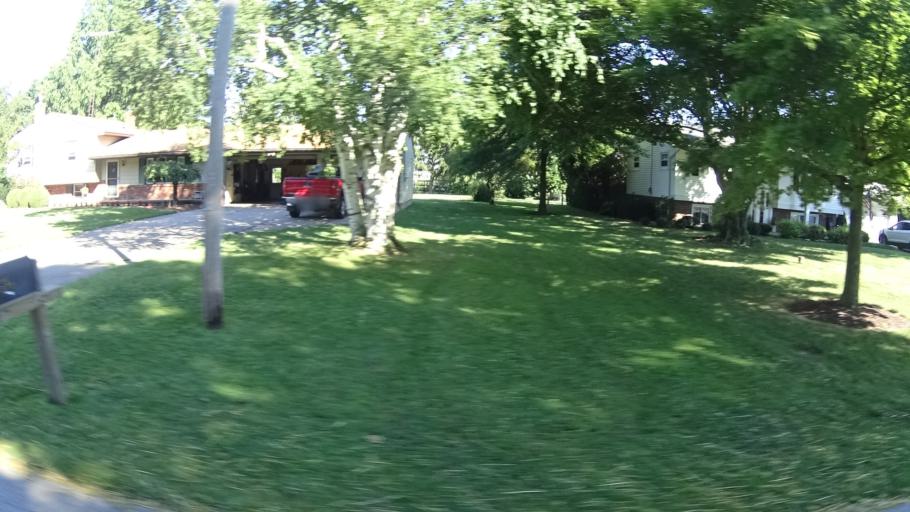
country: US
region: Ohio
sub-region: Erie County
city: Huron
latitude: 41.3625
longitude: -82.5958
